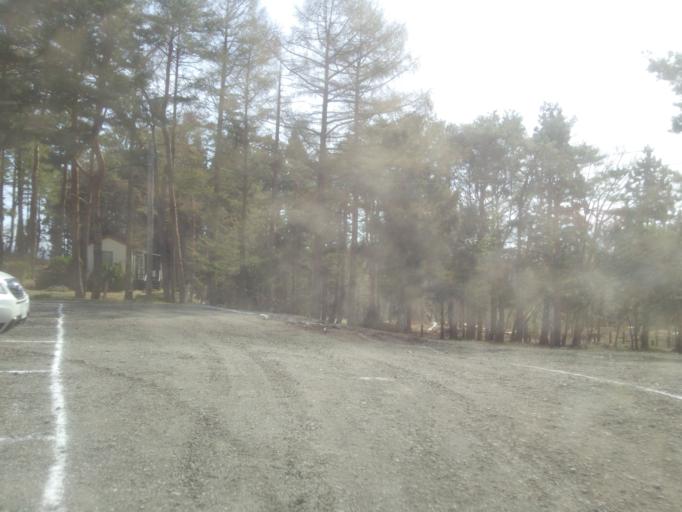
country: JP
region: Fukushima
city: Inawashiro
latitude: 37.5363
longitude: 140.0383
